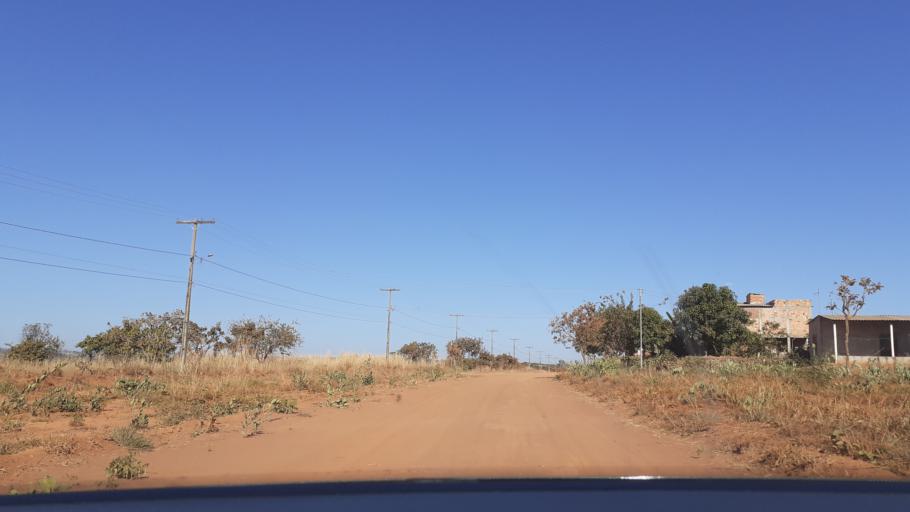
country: BR
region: Goias
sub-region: Aparecida De Goiania
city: Aparecida de Goiania
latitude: -16.8725
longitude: -49.2725
